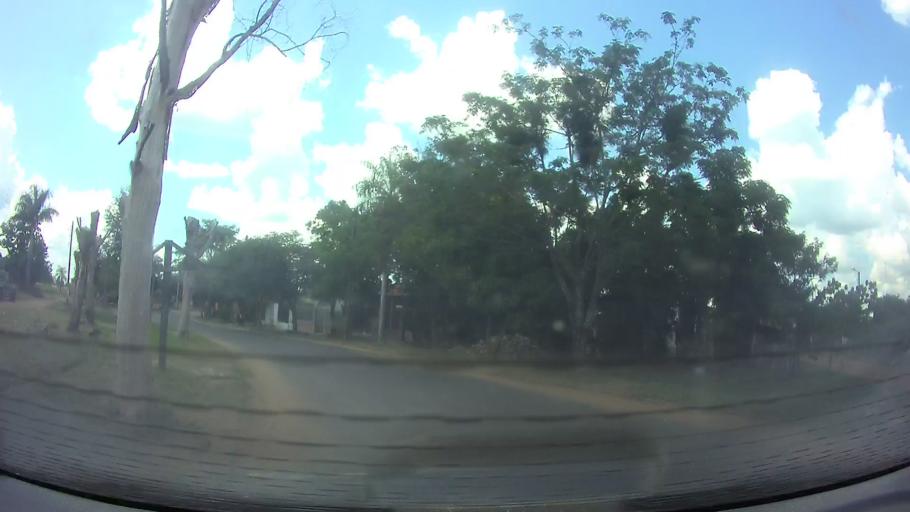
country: PY
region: Central
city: Limpio
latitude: -25.1658
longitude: -57.4316
